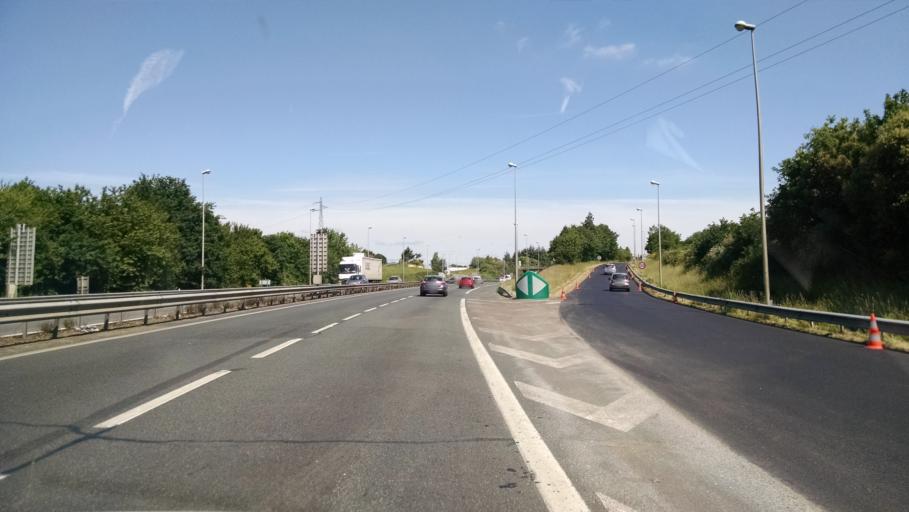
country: FR
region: Pays de la Loire
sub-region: Departement de la Loire-Atlantique
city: Saint-Herblain
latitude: 47.2077
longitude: -1.6259
